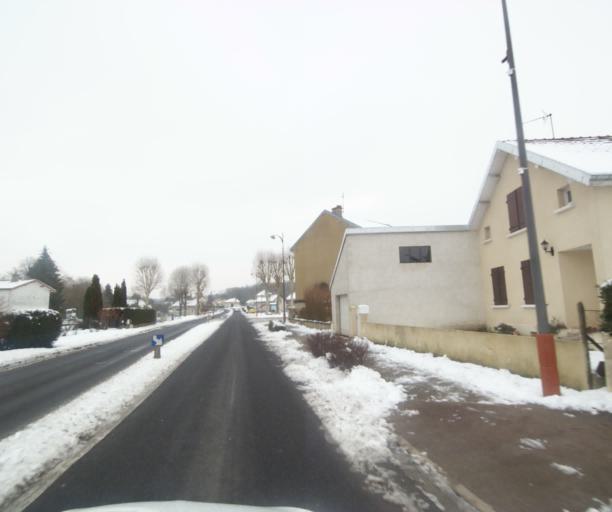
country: FR
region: Champagne-Ardenne
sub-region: Departement de la Haute-Marne
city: Saint-Dizier
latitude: 48.6174
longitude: 4.9042
